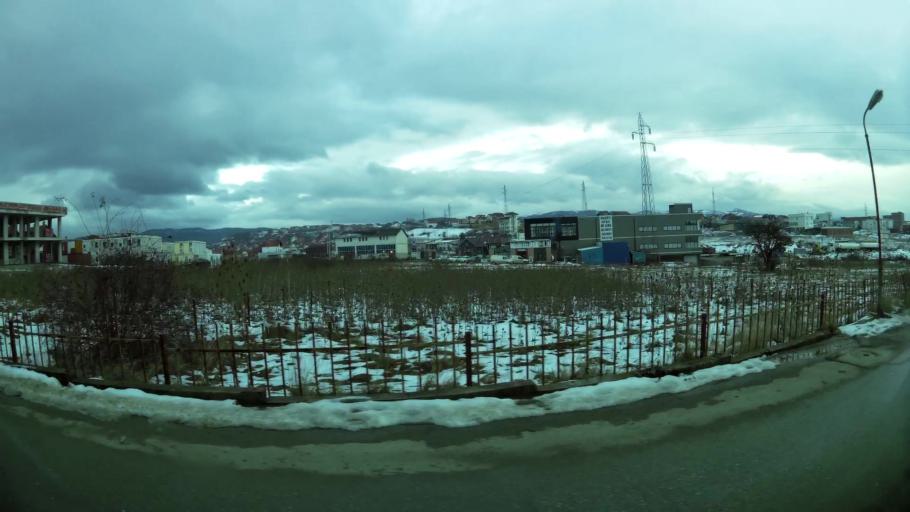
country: XK
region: Pristina
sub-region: Komuna e Prishtines
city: Pristina
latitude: 42.6197
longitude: 21.1668
